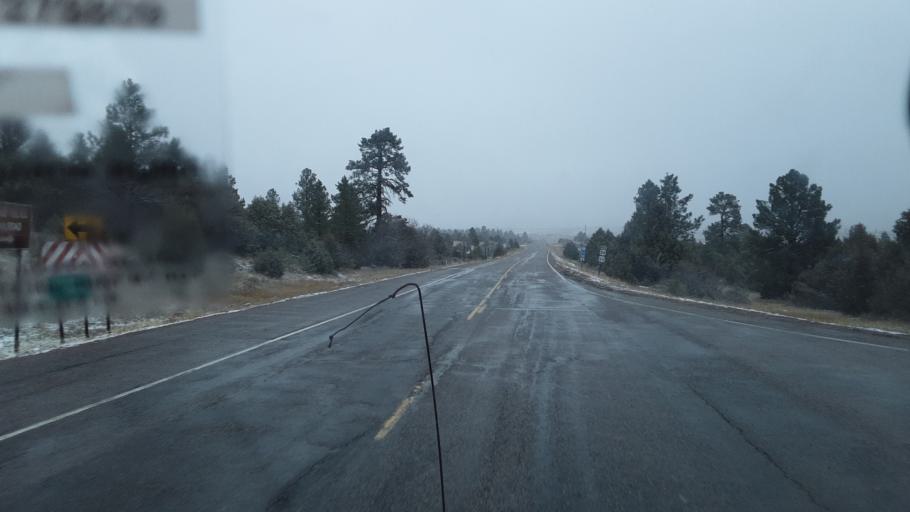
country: US
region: New Mexico
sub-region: Rio Arriba County
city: Tierra Amarilla
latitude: 36.6882
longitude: -106.5581
